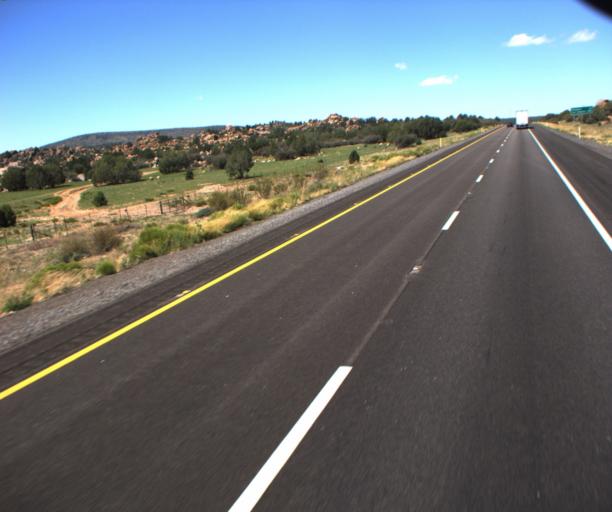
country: US
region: Arizona
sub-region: Mohave County
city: Peach Springs
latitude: 35.1909
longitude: -113.3785
